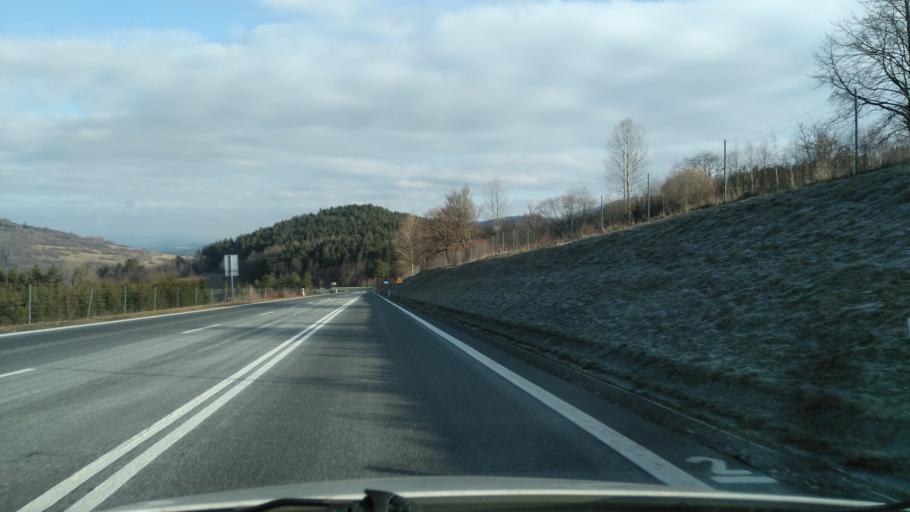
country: PL
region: Silesian Voivodeship
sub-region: Powiat zywiecki
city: Milowka
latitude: 49.5562
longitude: 19.0559
